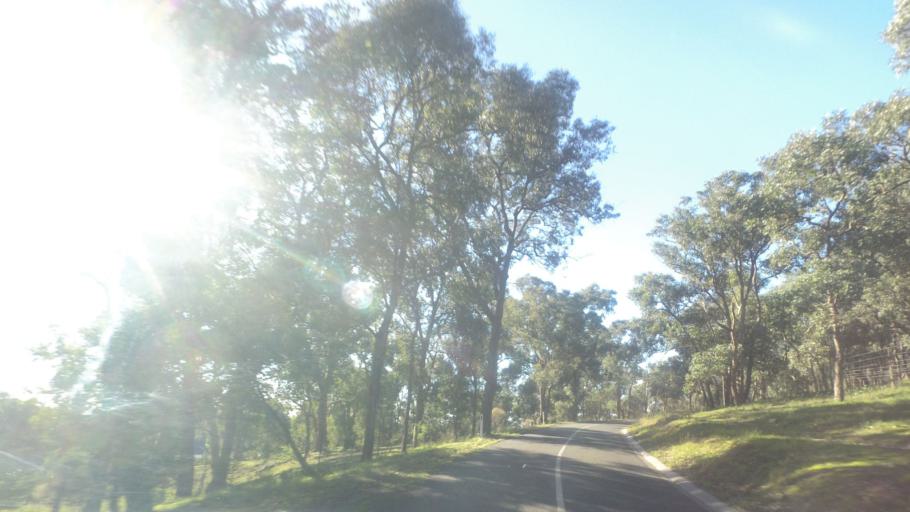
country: AU
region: Victoria
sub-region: Nillumbik
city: Research
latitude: -37.6925
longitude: 145.1962
